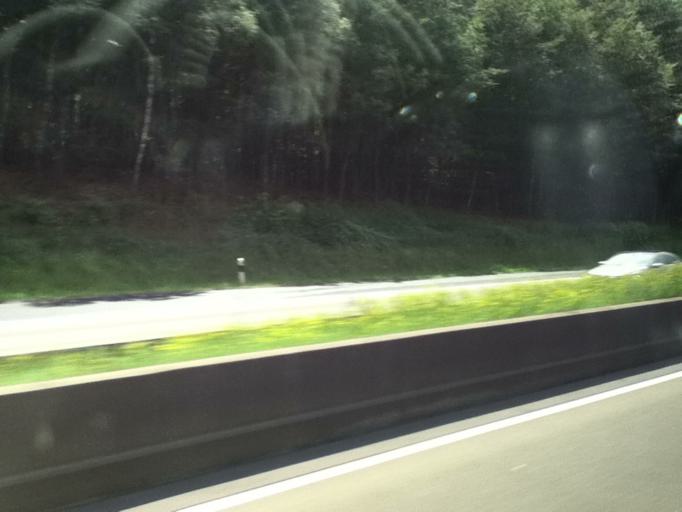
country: DE
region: Hesse
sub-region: Regierungsbezirk Kassel
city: Kirchheim
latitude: 50.8079
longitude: 9.5317
